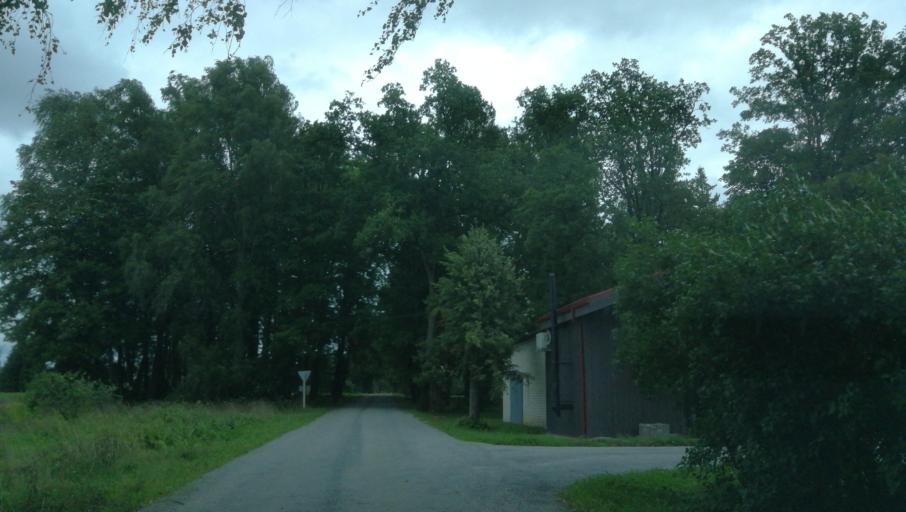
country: LV
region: Beverina
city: Murmuiza
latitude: 57.4946
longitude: 25.4478
